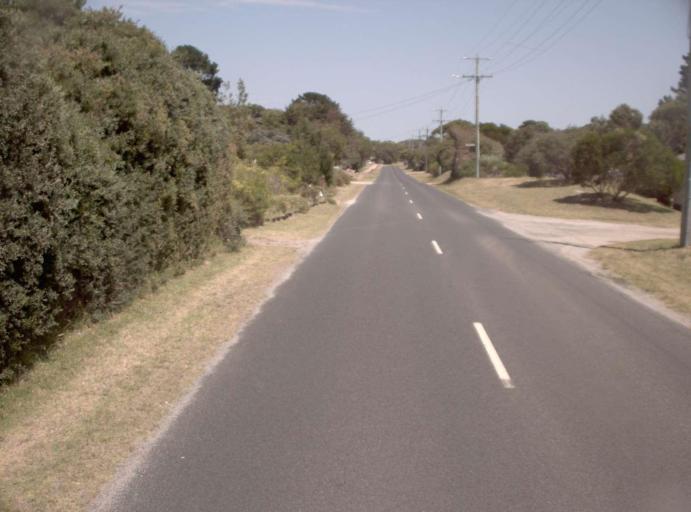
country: AU
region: Victoria
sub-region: Bass Coast
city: North Wonthaggi
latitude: -38.7024
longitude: 145.8289
